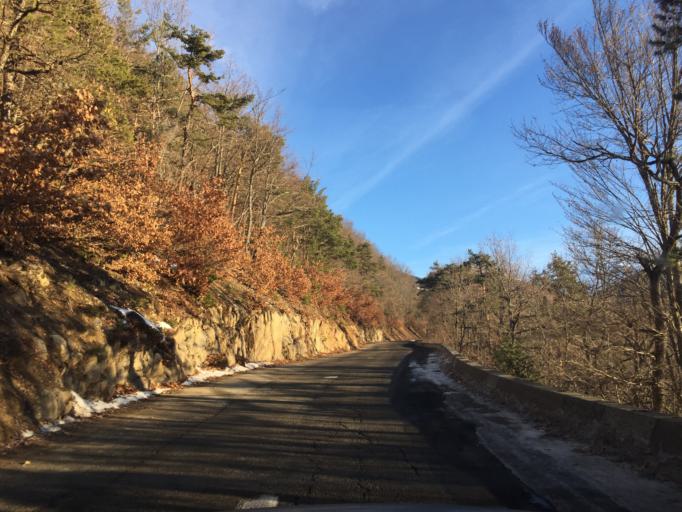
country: FR
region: Rhone-Alpes
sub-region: Departement de la Savoie
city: Aigueblanche
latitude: 45.5331
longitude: 6.4890
